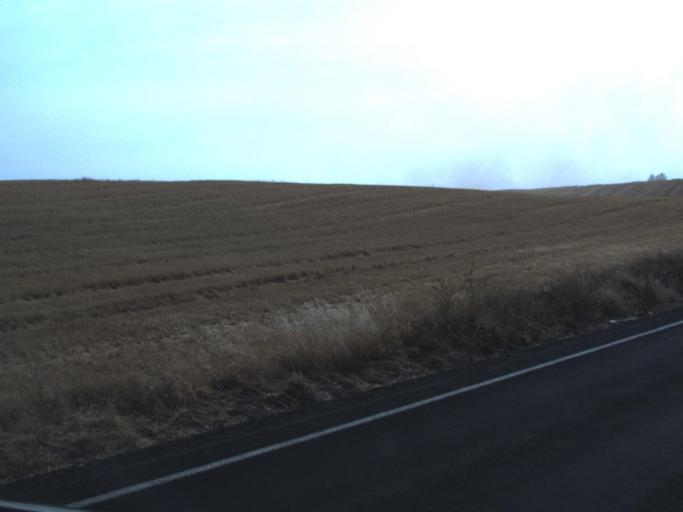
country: US
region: Washington
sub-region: Whitman County
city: Colfax
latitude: 47.0448
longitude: -117.1572
